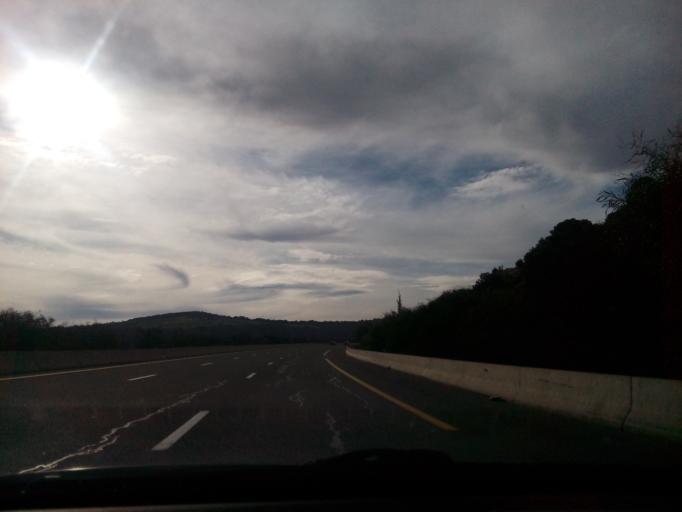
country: DZ
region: Sidi Bel Abbes
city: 'Ain el Berd
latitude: 35.3937
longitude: -0.4881
